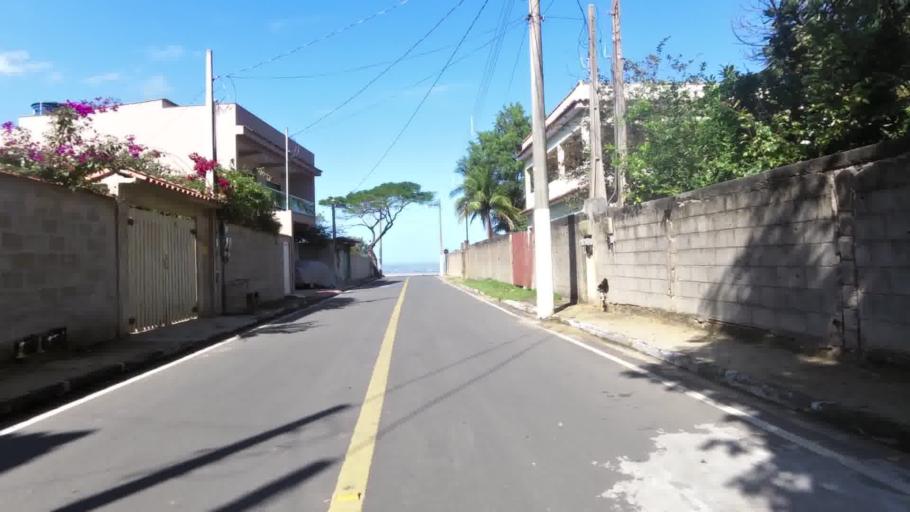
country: BR
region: Espirito Santo
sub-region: Piuma
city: Piuma
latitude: -20.8092
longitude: -40.6410
